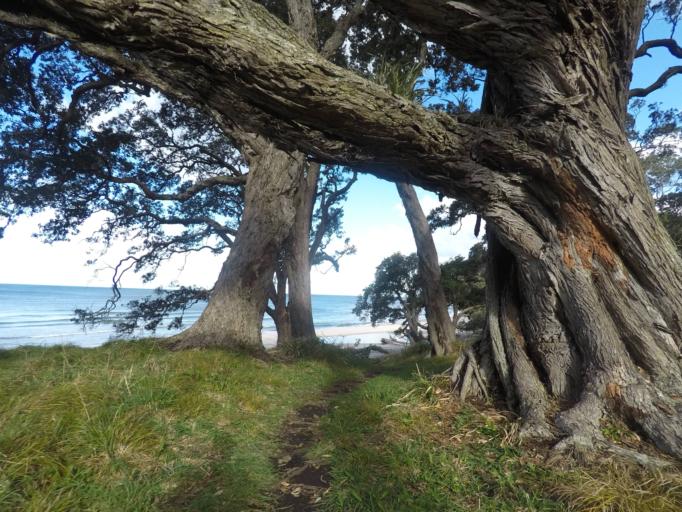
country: NZ
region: Bay of Plenty
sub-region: Western Bay of Plenty District
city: Waihi Beach
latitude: -37.3822
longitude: 175.9370
